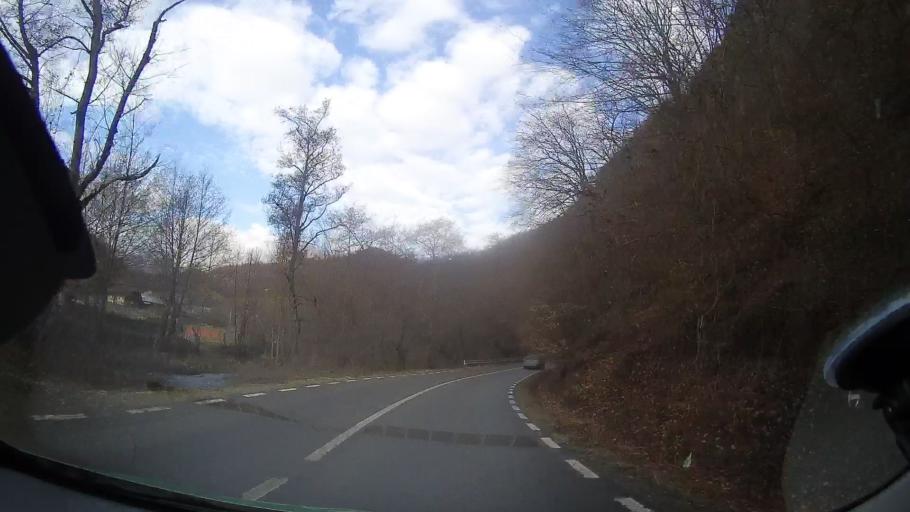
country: RO
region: Cluj
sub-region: Comuna Baisoara
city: Baisoara
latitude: 46.6031
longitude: 23.4247
